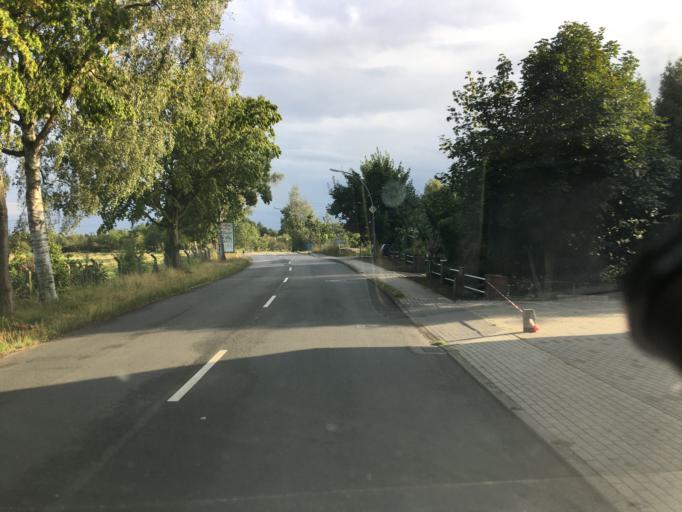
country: DE
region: Lower Saxony
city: Neu Wulmstorf
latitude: 53.4961
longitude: 9.8743
